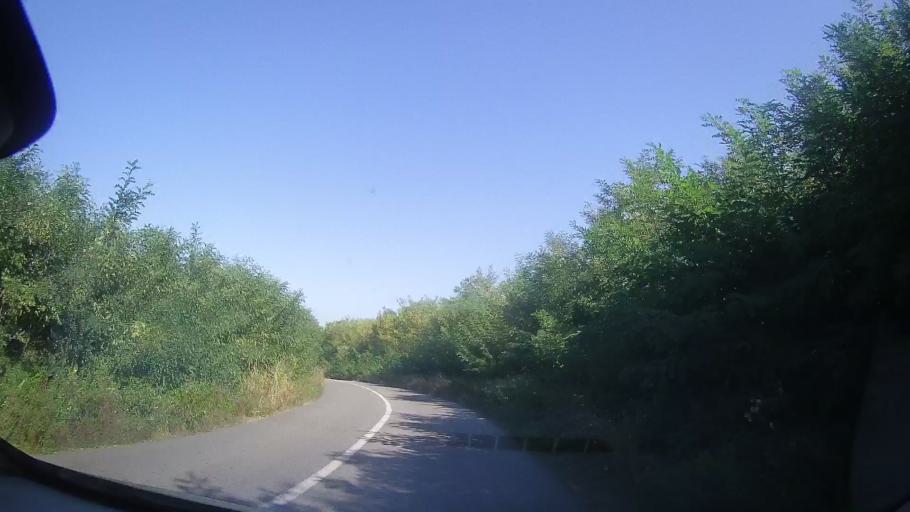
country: RO
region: Timis
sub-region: Comuna Balint
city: Balint
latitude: 45.8347
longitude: 21.8562
